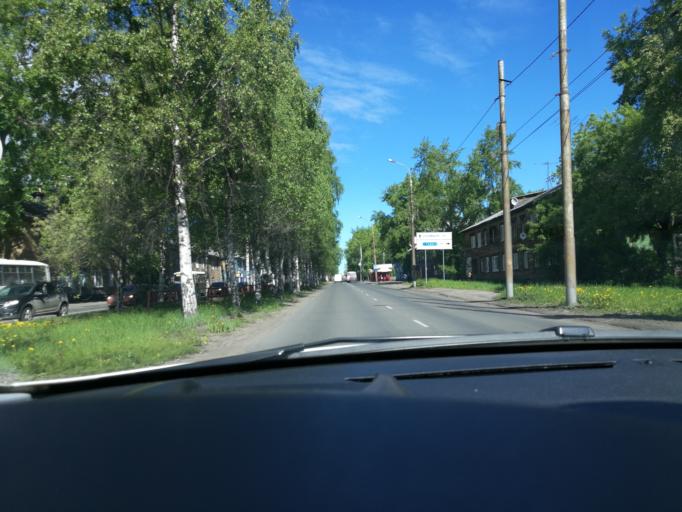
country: RU
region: Arkhangelskaya
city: Arkhangel'sk
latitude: 64.5582
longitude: 40.5504
